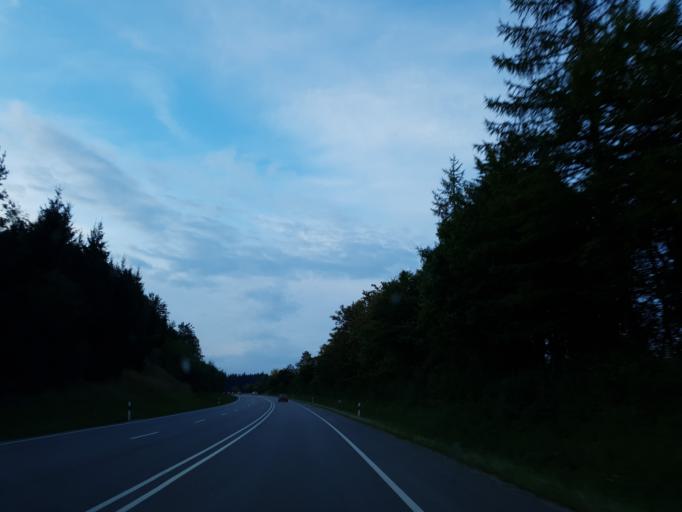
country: DE
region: Bavaria
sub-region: Swabia
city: Biessenhofen
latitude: 47.8402
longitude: 10.6756
